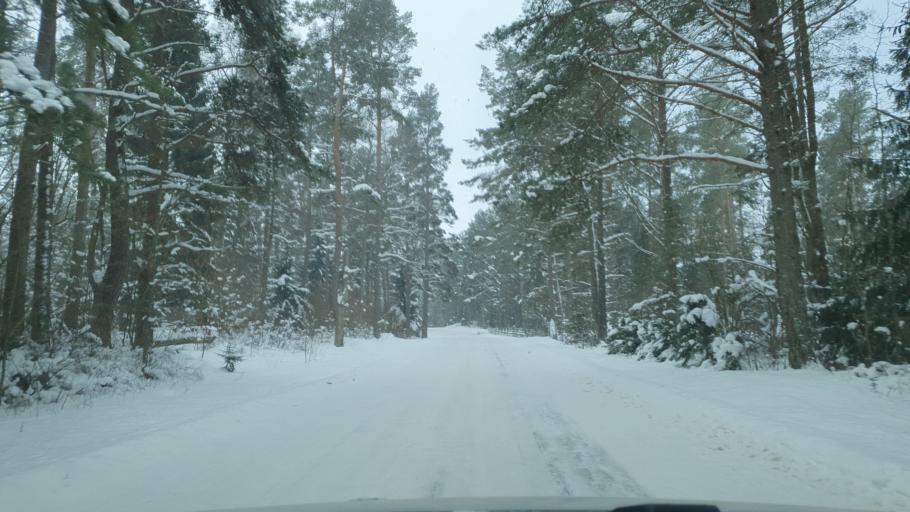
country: EE
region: Harju
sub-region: Kuusalu vald
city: Kuusalu
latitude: 59.4927
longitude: 25.3682
